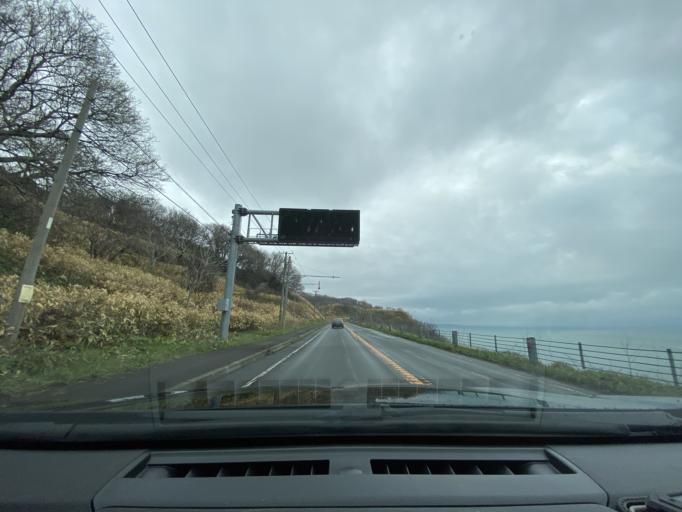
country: JP
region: Hokkaido
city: Ishikari
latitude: 43.4169
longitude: 141.4299
